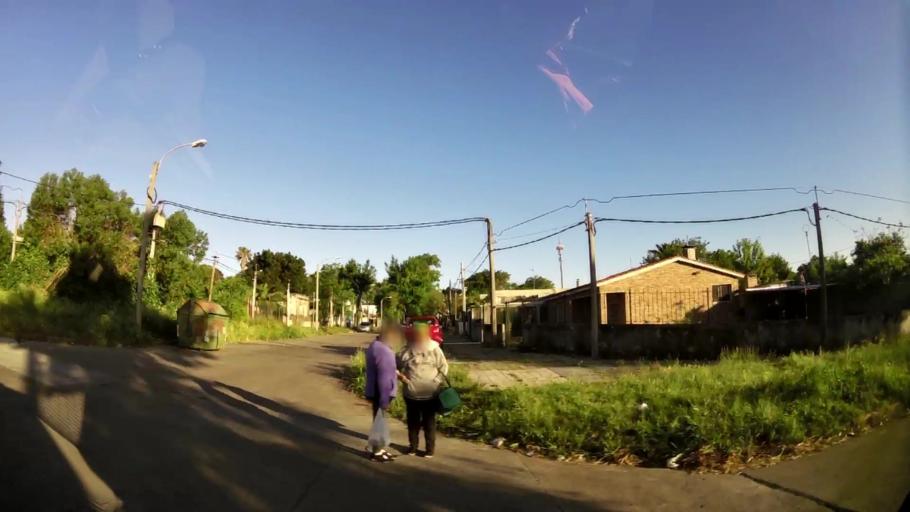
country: UY
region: Montevideo
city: Montevideo
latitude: -34.8445
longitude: -56.2135
